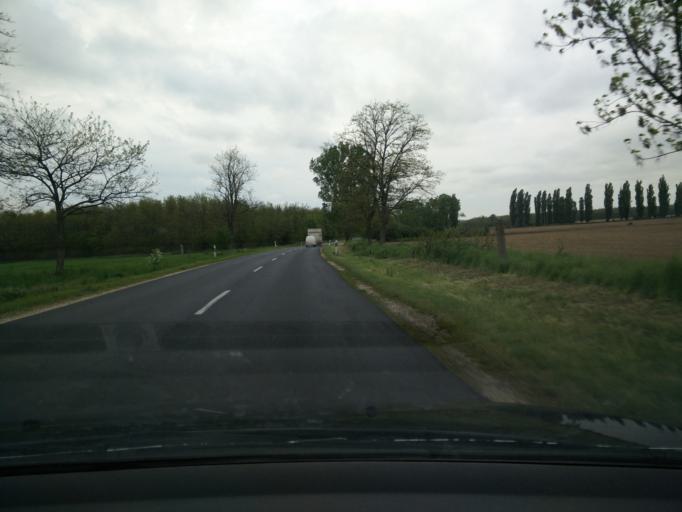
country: HU
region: Gyor-Moson-Sopron
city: Tet
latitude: 47.5361
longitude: 17.5339
